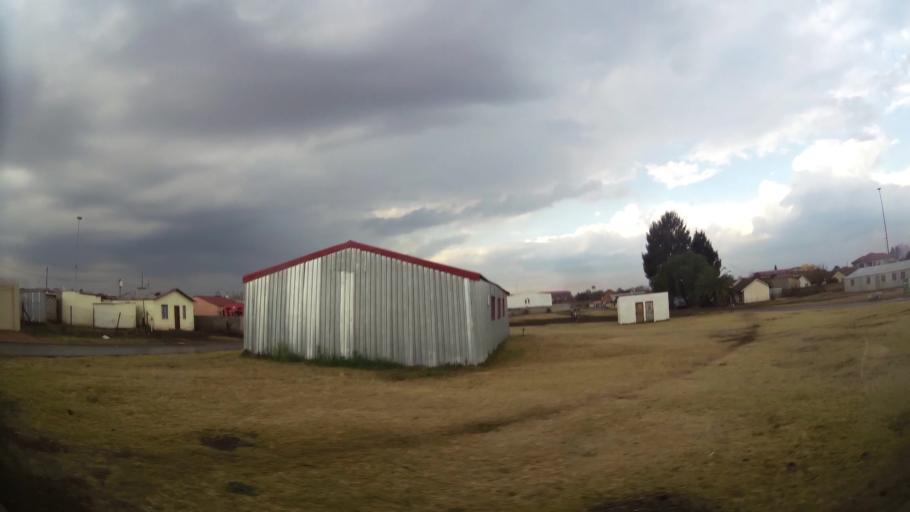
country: ZA
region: Gauteng
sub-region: Ekurhuleni Metropolitan Municipality
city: Germiston
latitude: -26.3691
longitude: 28.1298
